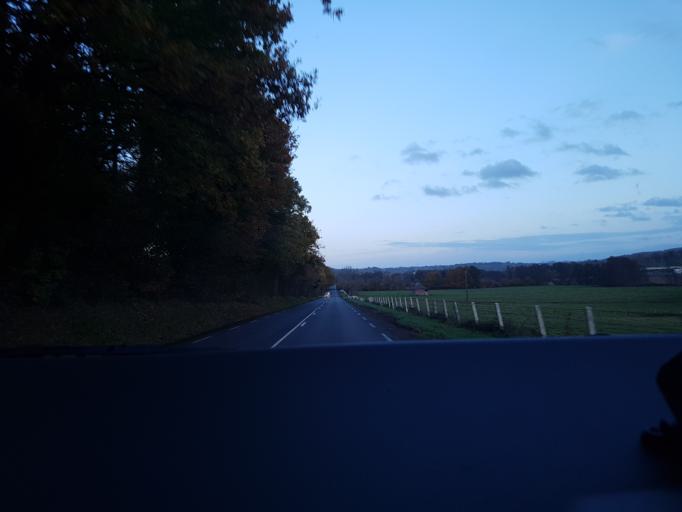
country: FR
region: Lower Normandy
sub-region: Departement du Calvados
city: Saint-Gatien-des-Bois
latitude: 49.3014
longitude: 0.2373
